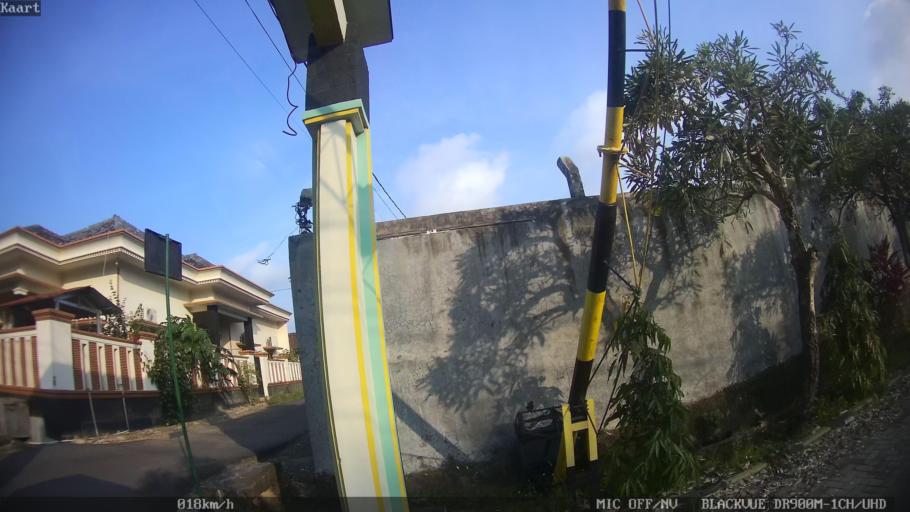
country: ID
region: Lampung
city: Kedaton
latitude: -5.4000
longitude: 105.2980
